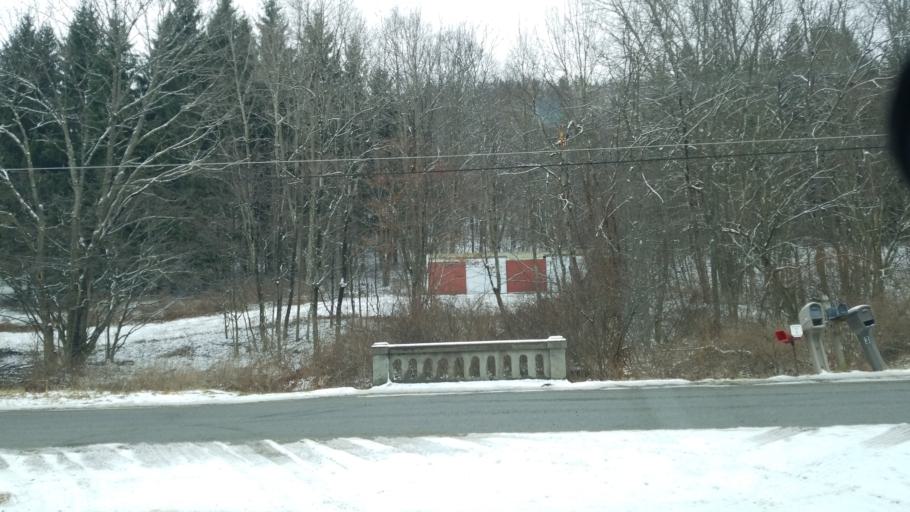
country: US
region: Pennsylvania
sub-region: Jefferson County
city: Sykesville
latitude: 41.0613
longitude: -78.8230
